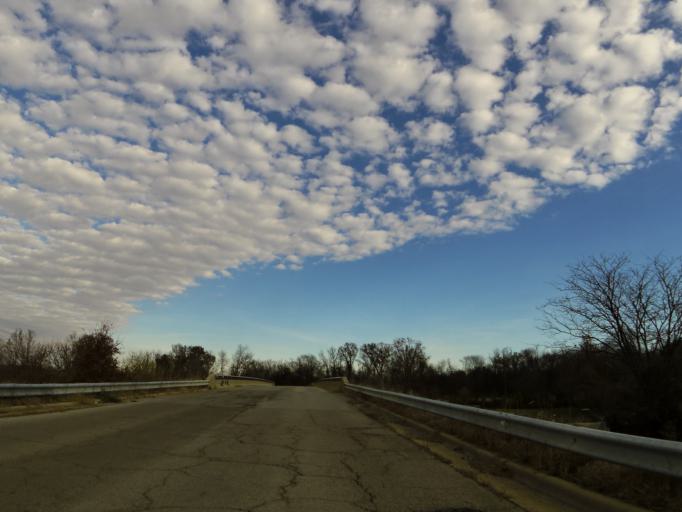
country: US
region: Illinois
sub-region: Jefferson County
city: Mount Vernon
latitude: 38.3419
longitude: -88.9696
